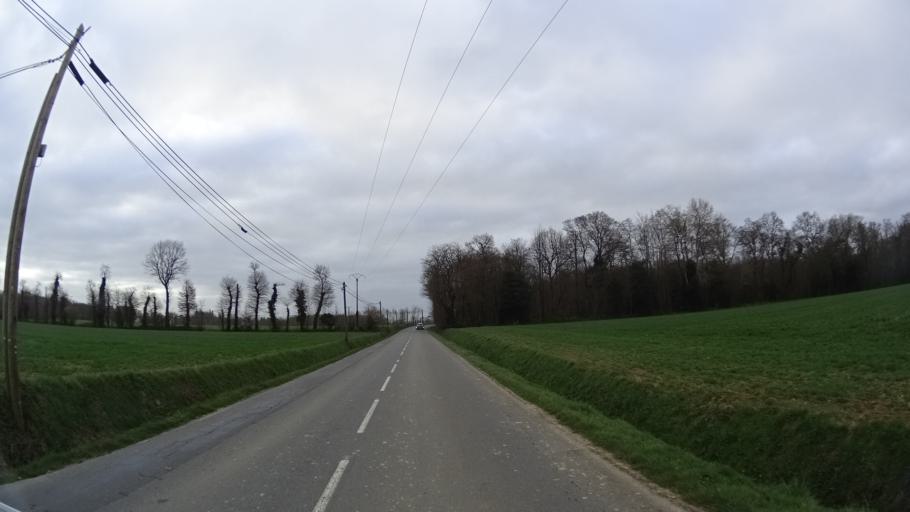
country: FR
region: Brittany
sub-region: Departement d'Ille-et-Vilaine
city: Saint-Gilles
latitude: 48.1793
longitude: -1.8491
